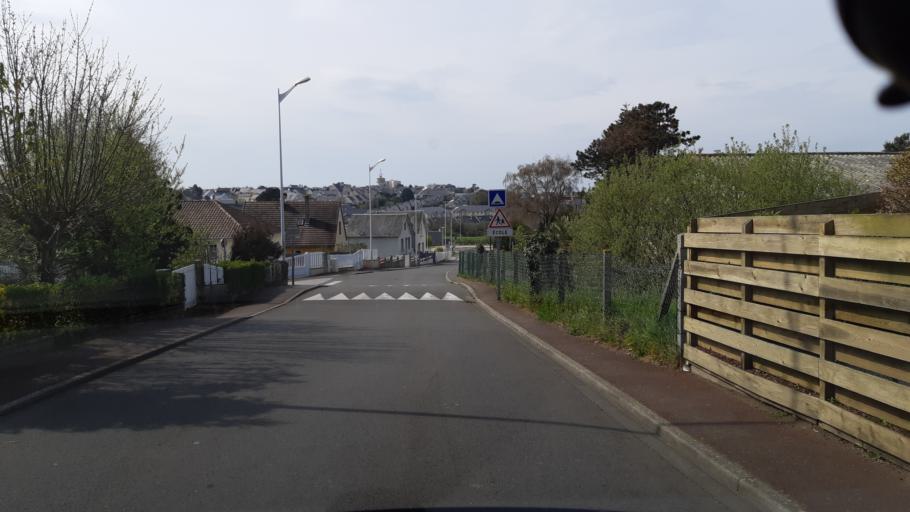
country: FR
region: Lower Normandy
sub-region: Departement de la Manche
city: Donville-les-Bains
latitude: 48.8469
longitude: -1.5746
